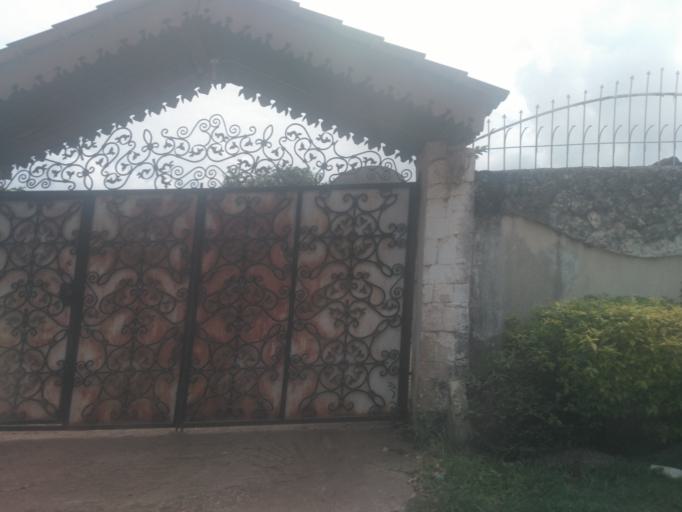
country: TZ
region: Zanzibar Urban/West
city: Zanzibar
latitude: -6.2246
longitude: 39.2141
